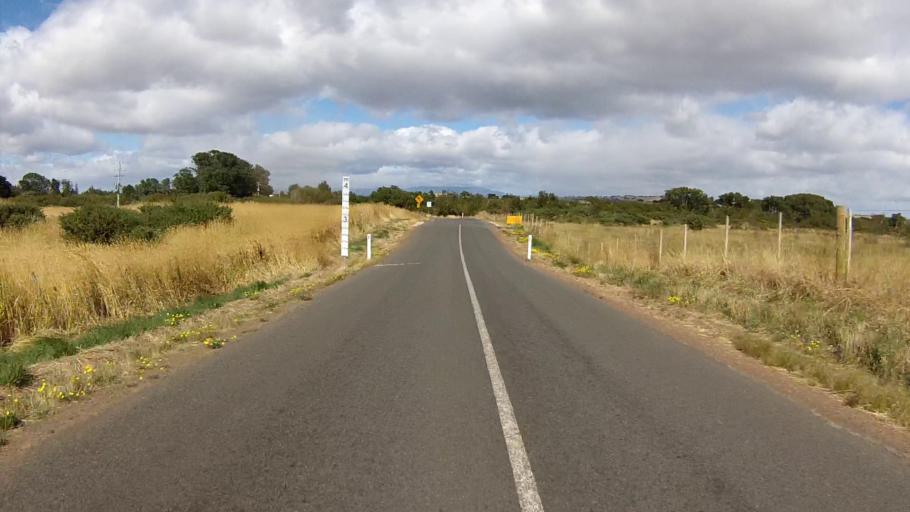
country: AU
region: Tasmania
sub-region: Northern Midlands
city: Evandale
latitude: -41.7688
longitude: 147.4786
